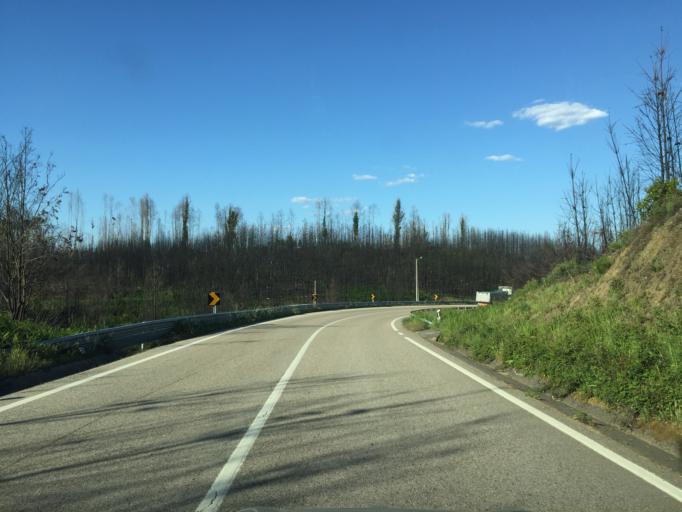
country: PT
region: Leiria
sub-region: Pedrogao Grande
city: Pedrogao Grande
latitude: 39.9790
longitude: -8.1377
